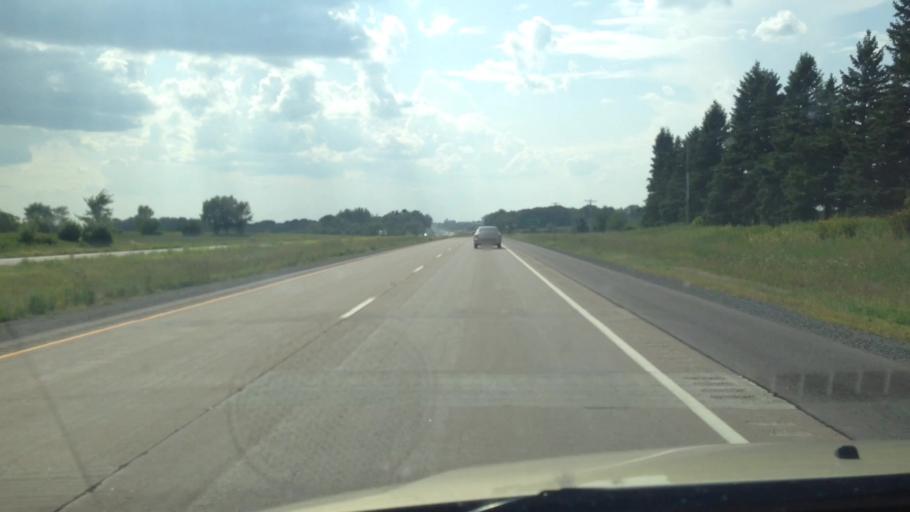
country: US
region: Wisconsin
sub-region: Clark County
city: Thorp
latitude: 44.9518
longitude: -90.8164
